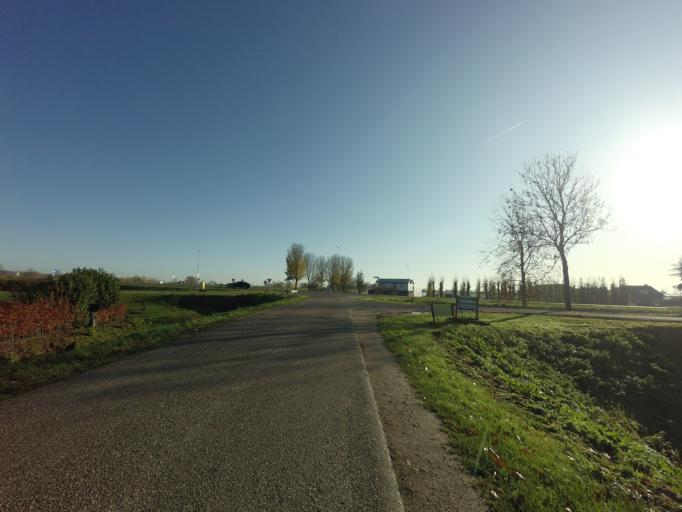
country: NL
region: Gelderland
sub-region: Gemeente Neerijnen
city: Neerijnen
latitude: 51.7877
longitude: 5.3170
